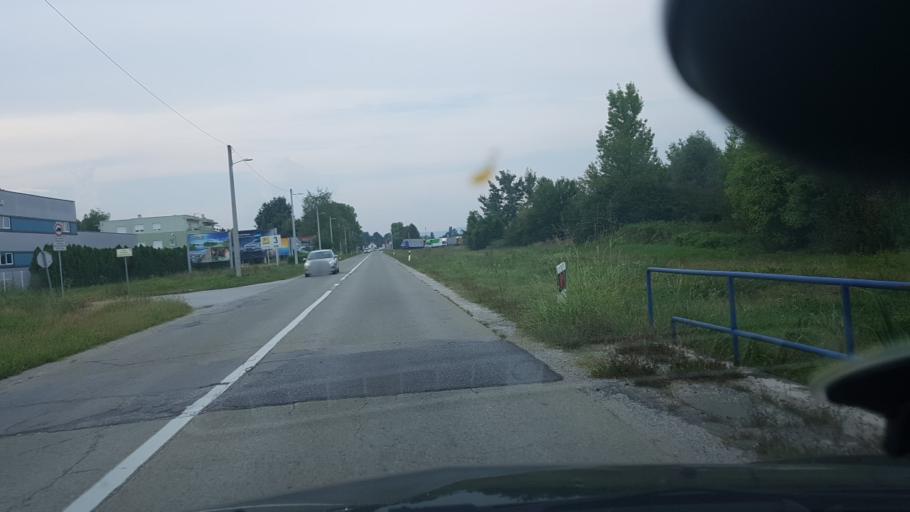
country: HR
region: Zagrebacka
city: Bregana
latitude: 45.8282
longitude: 15.7011
